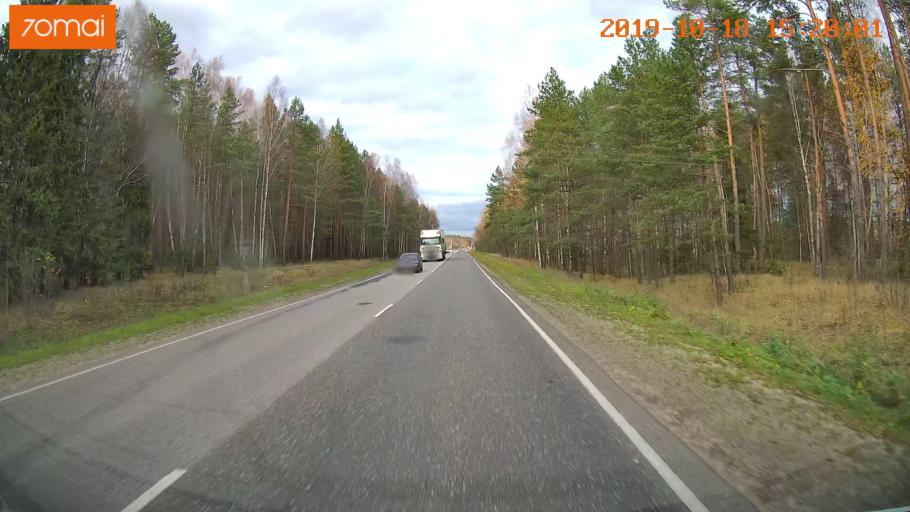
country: RU
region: Vladimir
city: Anopino
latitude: 55.6817
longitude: 40.7420
